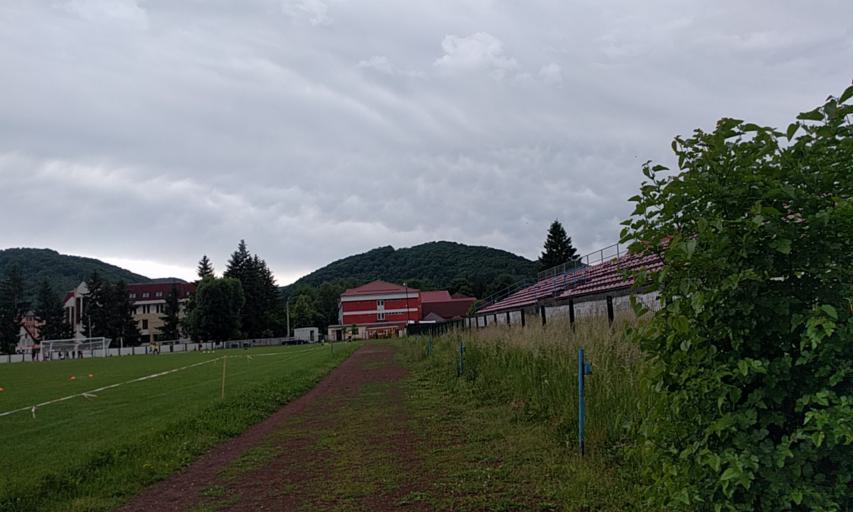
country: RO
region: Bistrita-Nasaud
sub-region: Oras Nasaud
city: Nasaud
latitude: 47.2858
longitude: 24.4117
